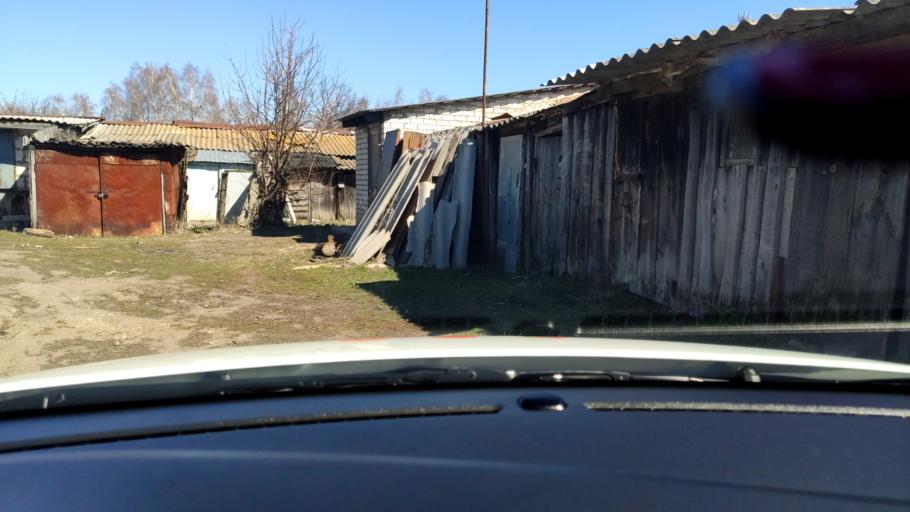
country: RU
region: Voronezj
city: Ramon'
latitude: 51.9843
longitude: 39.2221
